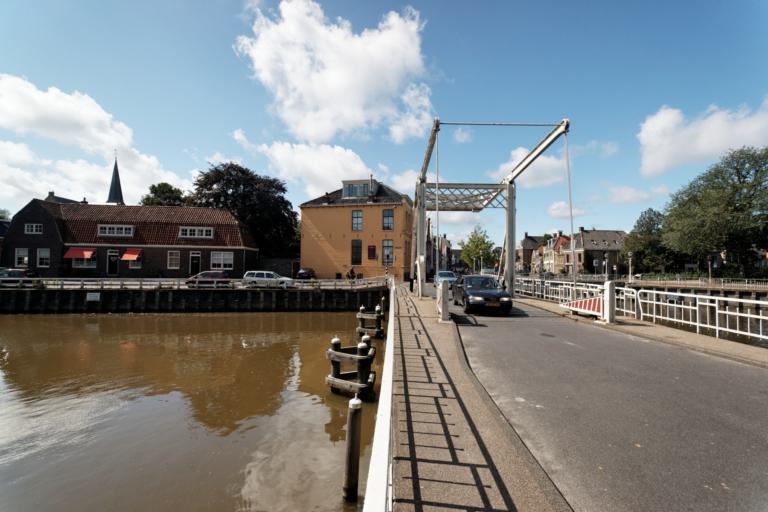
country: NL
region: Friesland
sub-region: Gemeente Harlingen
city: Harlingen
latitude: 53.1739
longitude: 5.4245
